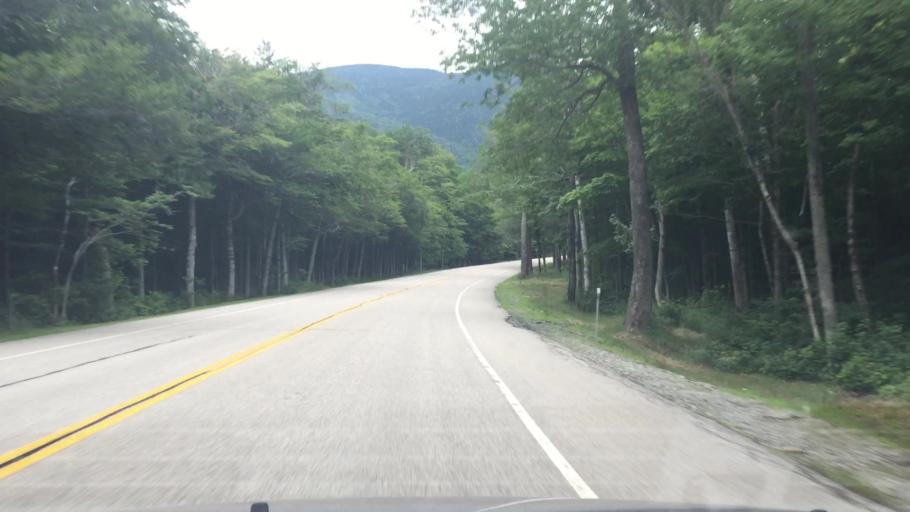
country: US
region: New Hampshire
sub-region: Grafton County
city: Deerfield
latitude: 44.1667
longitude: -71.3729
